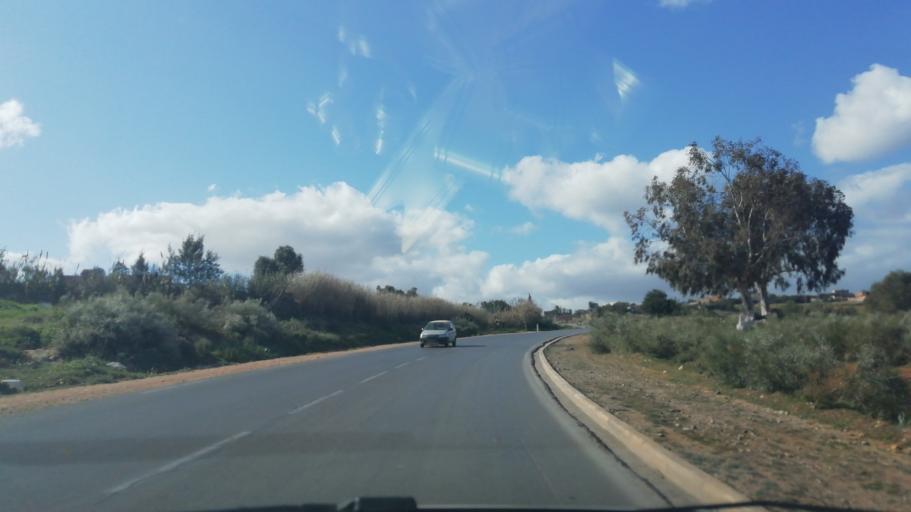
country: DZ
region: Relizane
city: Mazouna
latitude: 36.2903
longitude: 0.6513
